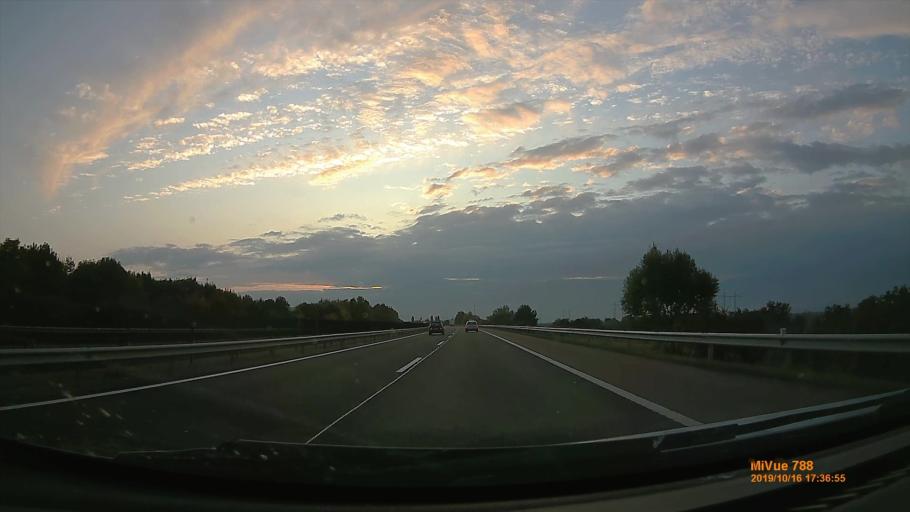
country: HU
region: Heves
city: Kompolt
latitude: 47.7126
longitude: 20.2044
